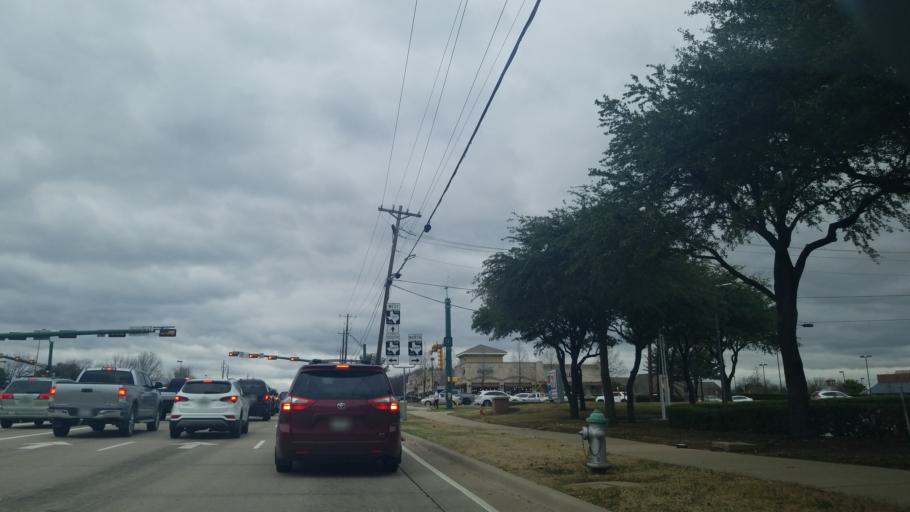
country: US
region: Texas
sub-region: Denton County
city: Flower Mound
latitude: 33.0360
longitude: -97.0694
